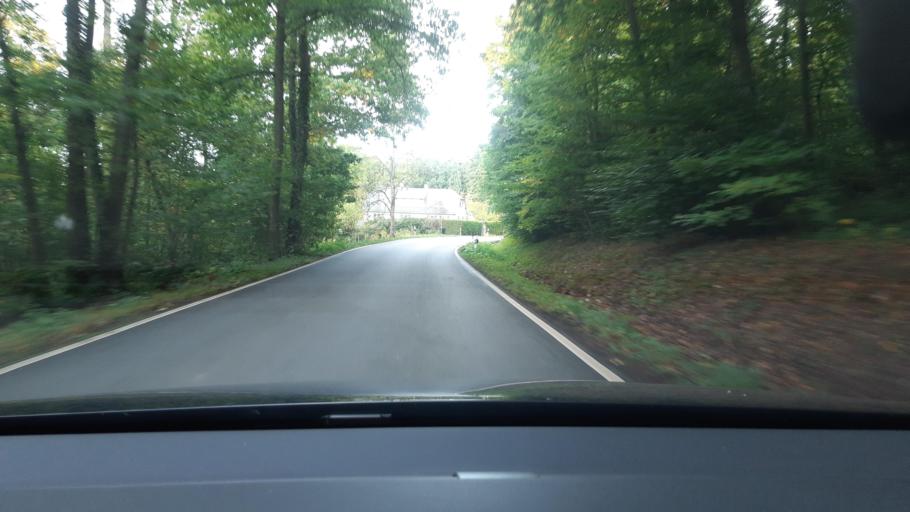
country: DE
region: Hesse
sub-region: Regierungsbezirk Giessen
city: Wetzlar
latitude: 50.5318
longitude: 8.5219
